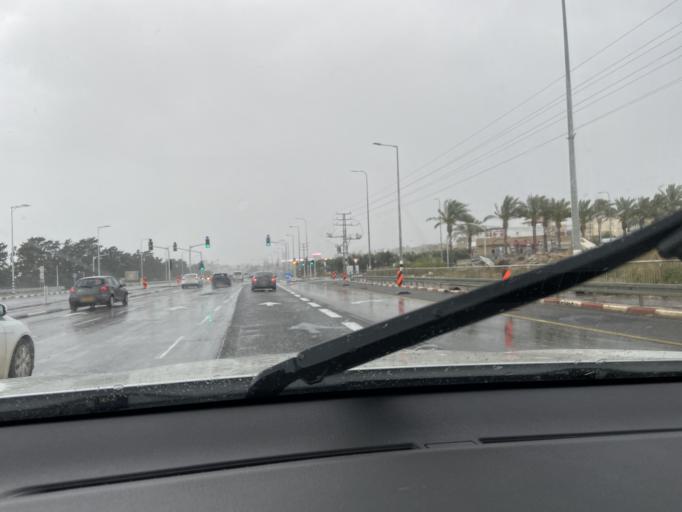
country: IL
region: Northern District
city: El Mazra`a
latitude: 32.9819
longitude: 35.0946
